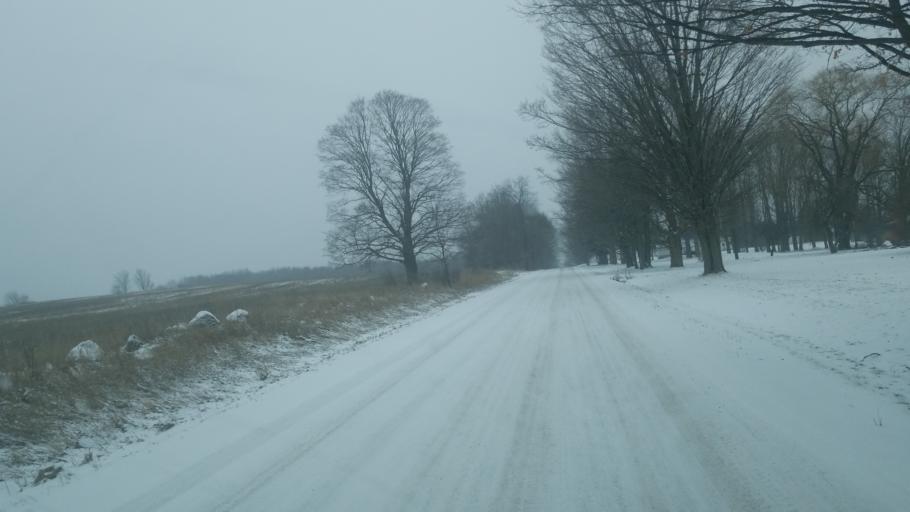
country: US
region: Michigan
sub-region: Osceola County
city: Reed City
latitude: 43.8408
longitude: -85.3940
